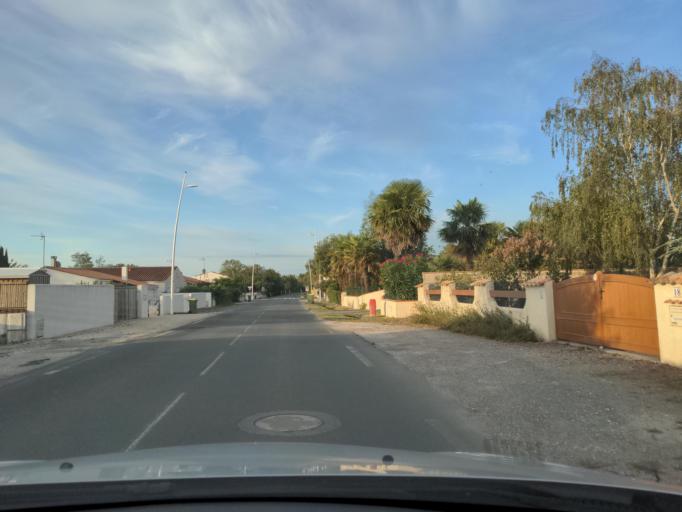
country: FR
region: Poitou-Charentes
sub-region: Departement de la Charente-Maritime
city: Saint-Trojan-les-Bains
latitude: 45.8832
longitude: -1.2115
